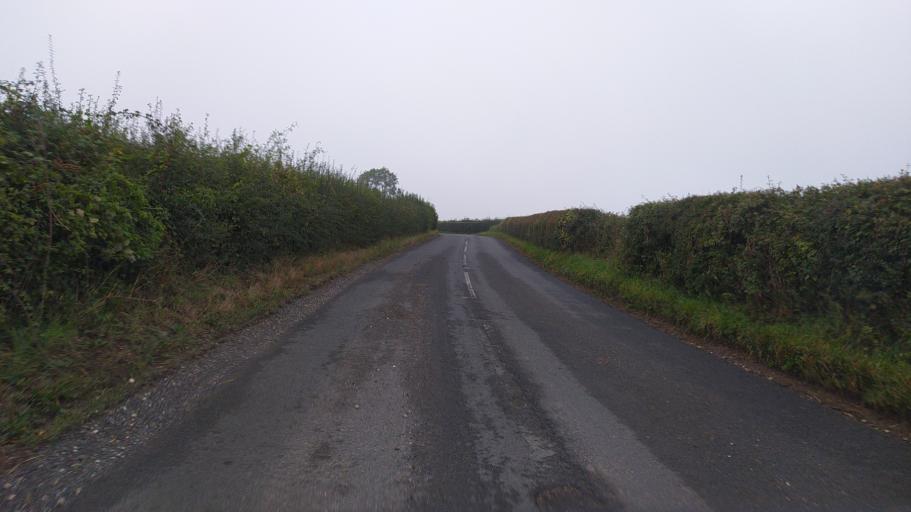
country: GB
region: England
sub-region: Wiltshire
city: Ansty
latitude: 50.9607
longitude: -2.1034
